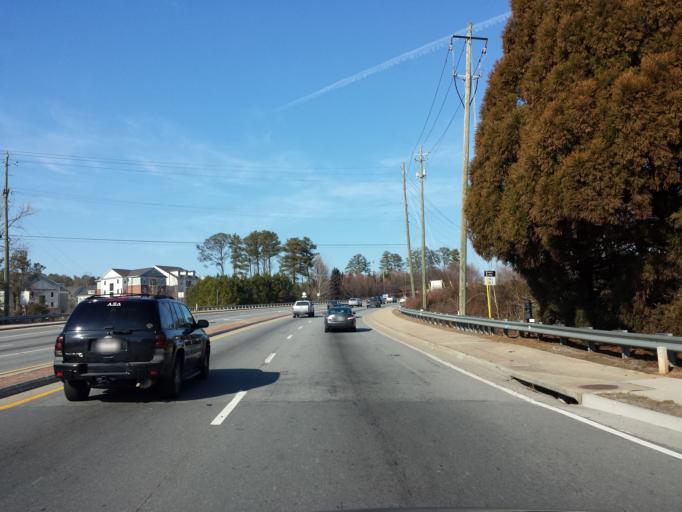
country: US
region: Georgia
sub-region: Cobb County
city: Kennesaw
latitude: 34.0295
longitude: -84.5837
